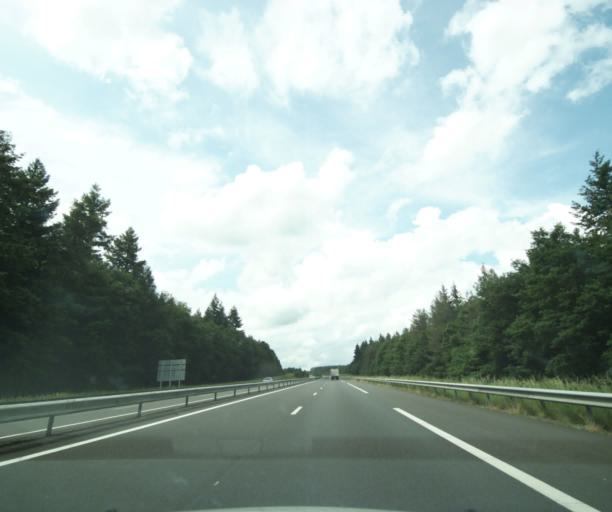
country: FR
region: Auvergne
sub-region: Departement de l'Allier
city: Bellenaves
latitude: 46.2432
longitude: 3.0922
